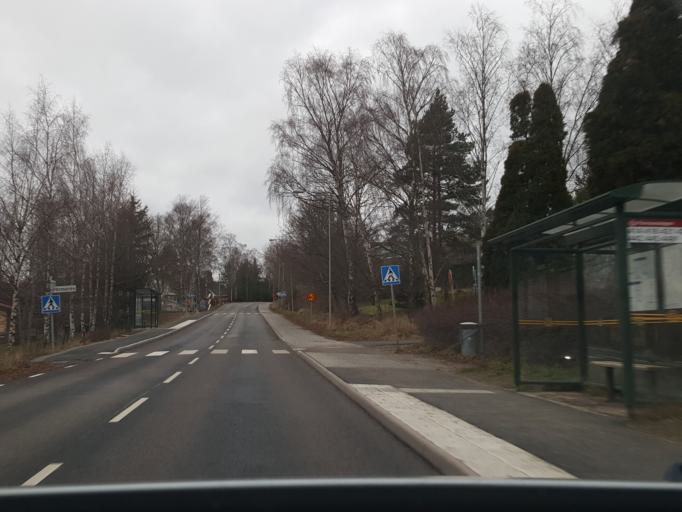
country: SE
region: Stockholm
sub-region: Nacka Kommun
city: Boo
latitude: 59.3298
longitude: 18.2798
